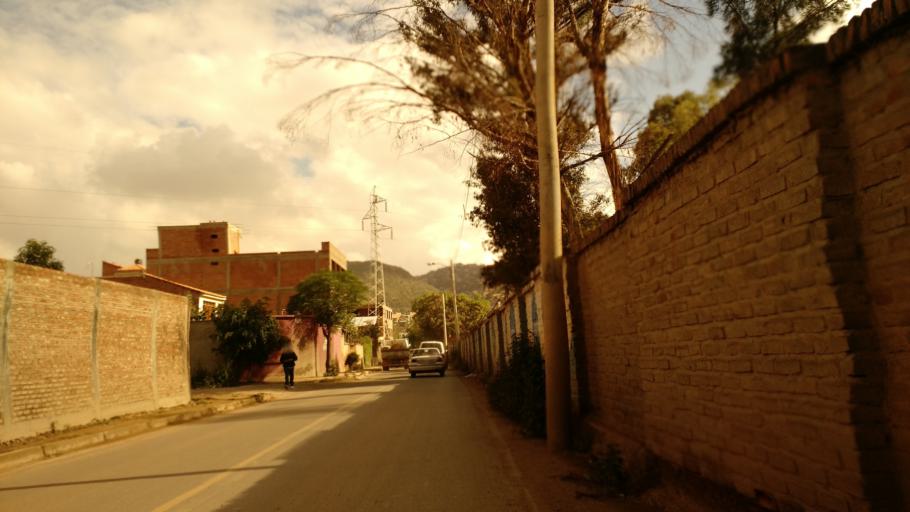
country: BO
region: Cochabamba
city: Cochabamba
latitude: -17.4495
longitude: -66.1410
